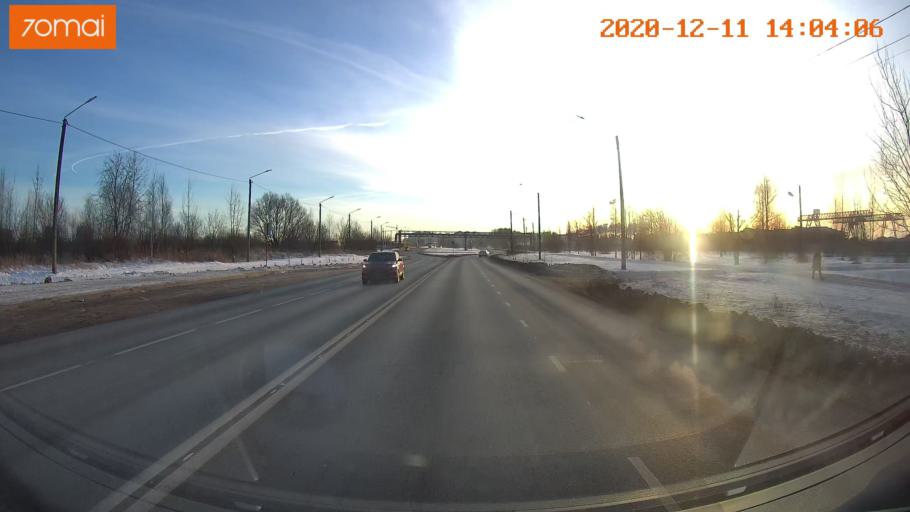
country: RU
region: Kostroma
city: Oktyabr'skiy
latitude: 57.7588
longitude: 41.0164
